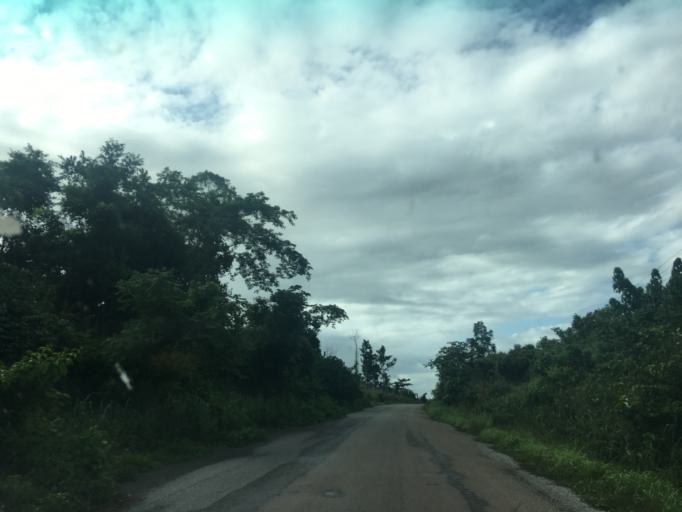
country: GH
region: Western
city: Wassa-Akropong
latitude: 6.0148
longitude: -2.4037
